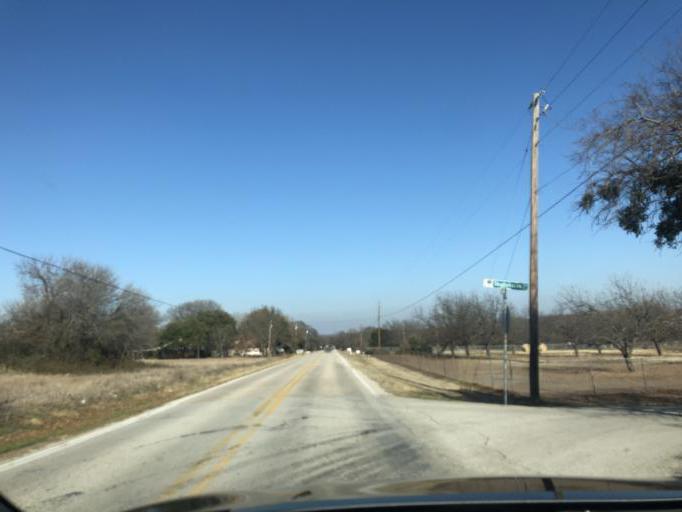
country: US
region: Texas
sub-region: Dallas County
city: Cedar Hill
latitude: 32.6123
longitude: -96.9386
